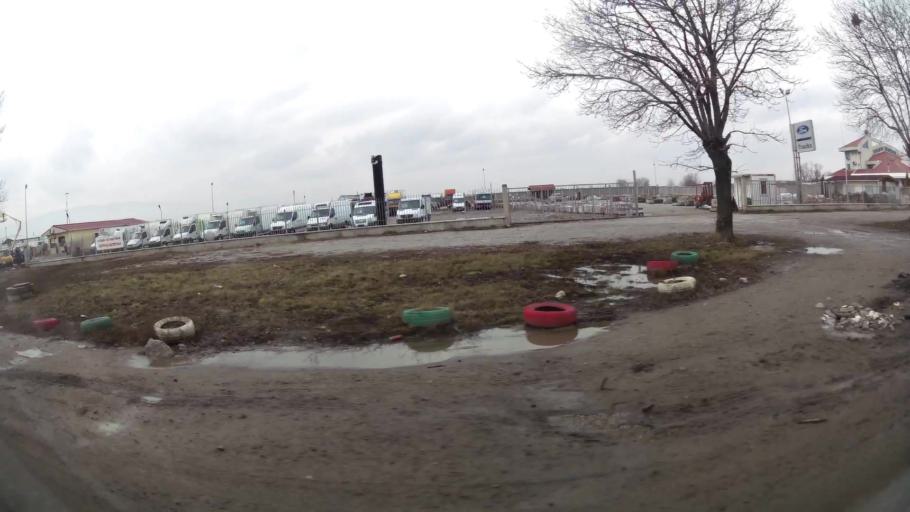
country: BG
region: Sofiya
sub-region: Obshtina Bozhurishte
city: Bozhurishte
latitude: 42.7053
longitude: 23.2303
